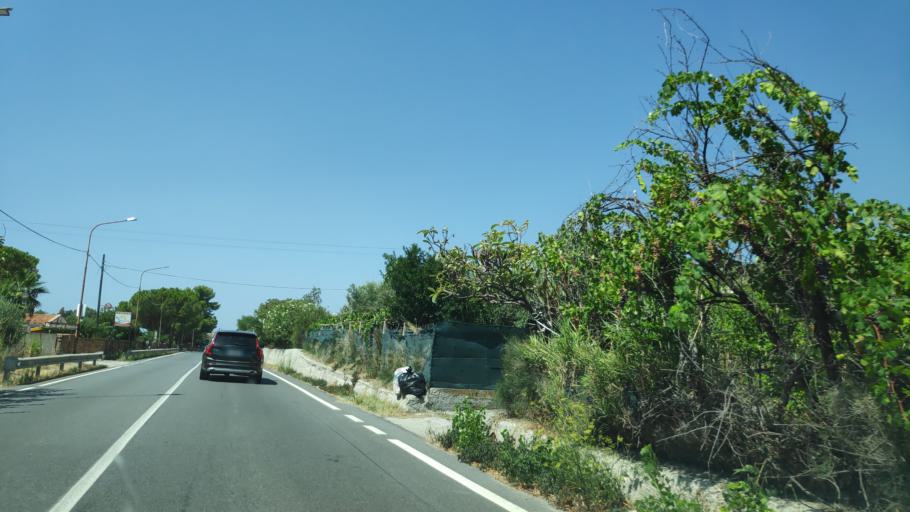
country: IT
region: Calabria
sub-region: Provincia di Reggio Calabria
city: Palizzi Marina
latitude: 37.9240
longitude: 16.0248
